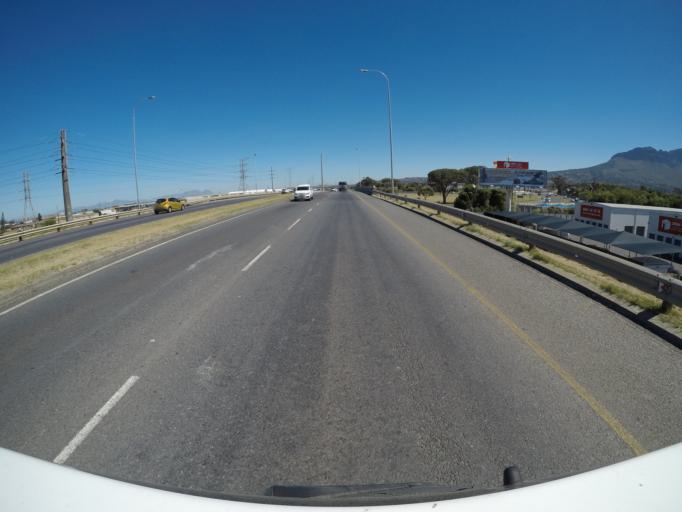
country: ZA
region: Western Cape
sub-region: Cape Winelands District Municipality
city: Stellenbosch
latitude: -34.1007
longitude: 18.8516
